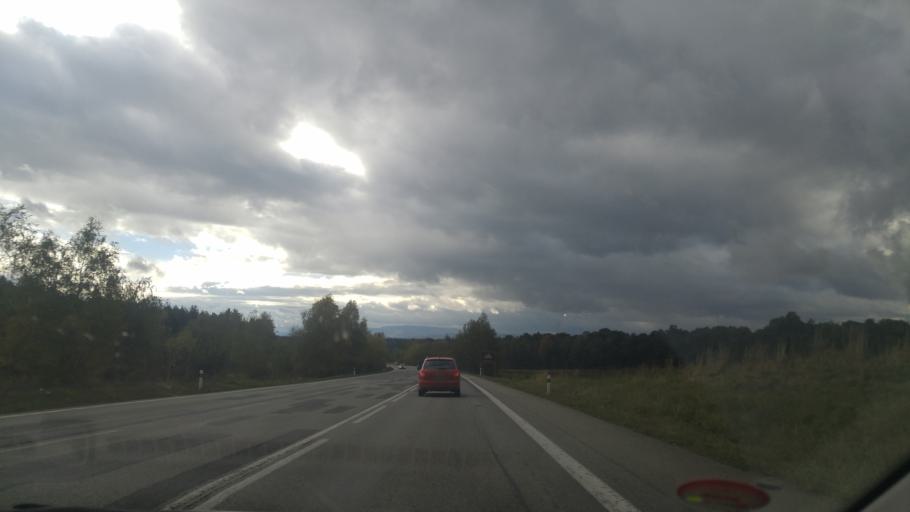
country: CZ
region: Jihocesky
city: Borek
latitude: 49.0632
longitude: 14.5260
